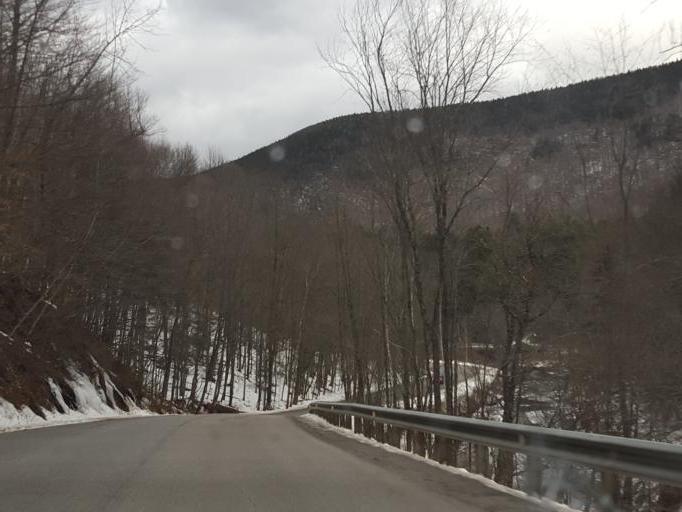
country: US
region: Vermont
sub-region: Rutland County
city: Rutland
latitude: 43.6113
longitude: -72.7566
